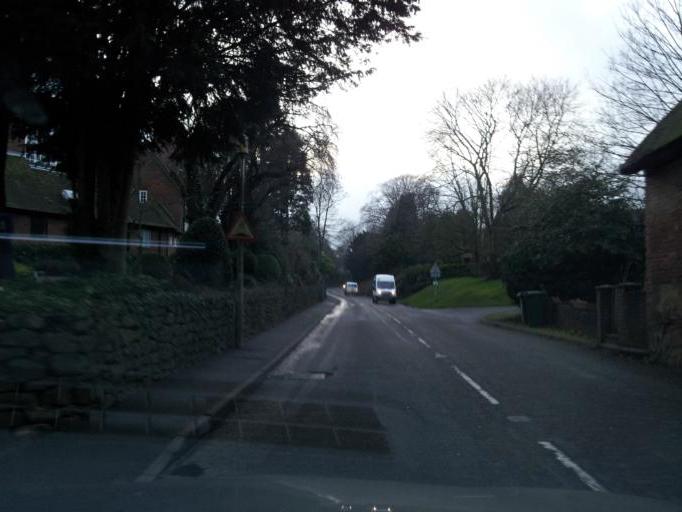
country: GB
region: England
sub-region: Derbyshire
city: Repton
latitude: 52.8389
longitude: -1.5516
